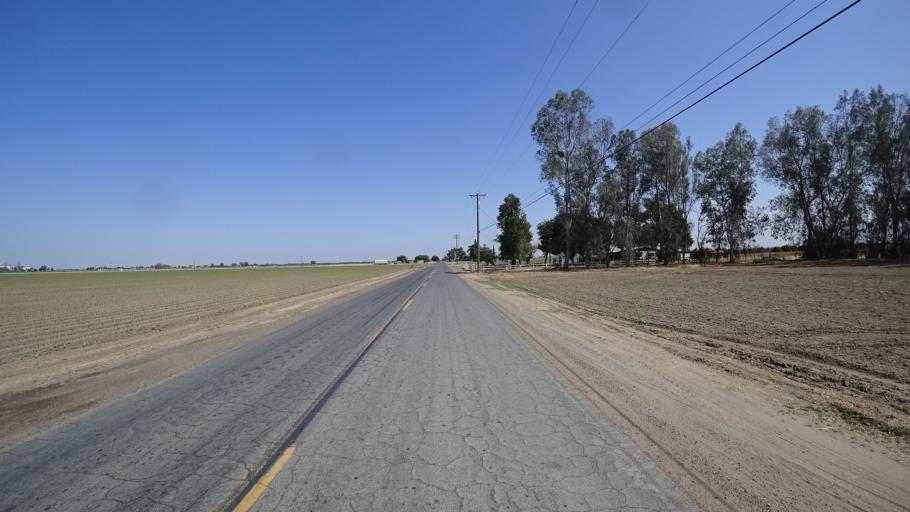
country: US
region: California
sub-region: Kings County
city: Home Garden
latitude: 36.2696
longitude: -119.6190
